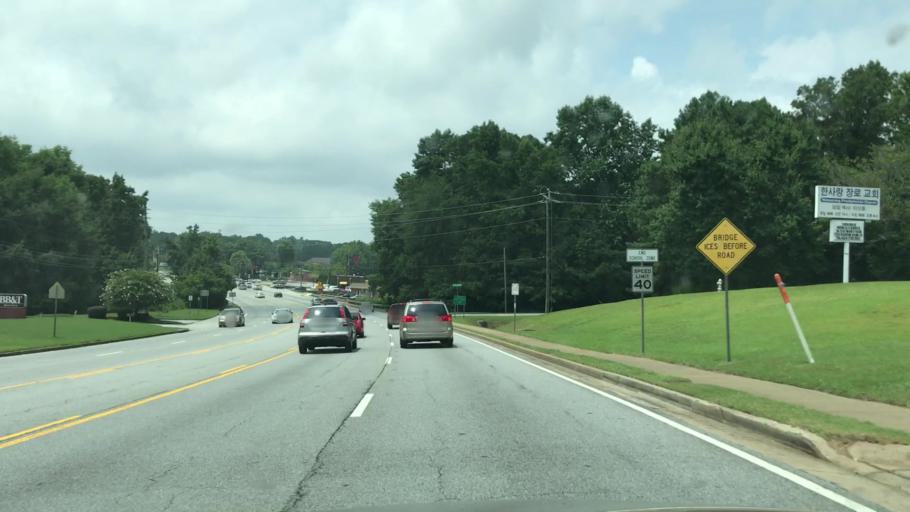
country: US
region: Georgia
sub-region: Gwinnett County
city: Lilburn
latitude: 33.8985
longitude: -84.1374
